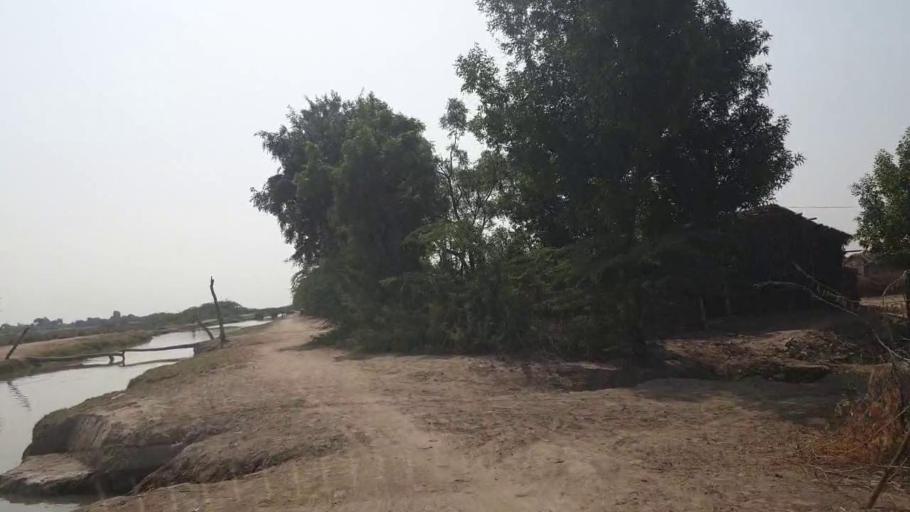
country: PK
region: Sindh
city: Kadhan
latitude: 24.5063
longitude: 68.8501
